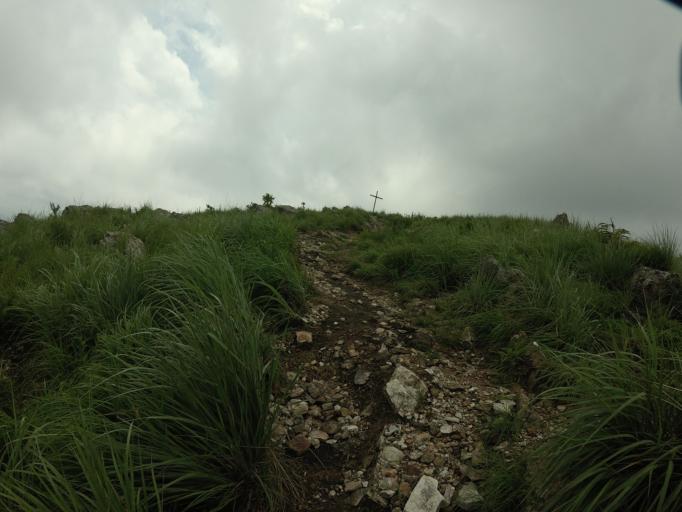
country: GH
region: Volta
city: Kpandu
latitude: 6.8552
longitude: 0.4334
